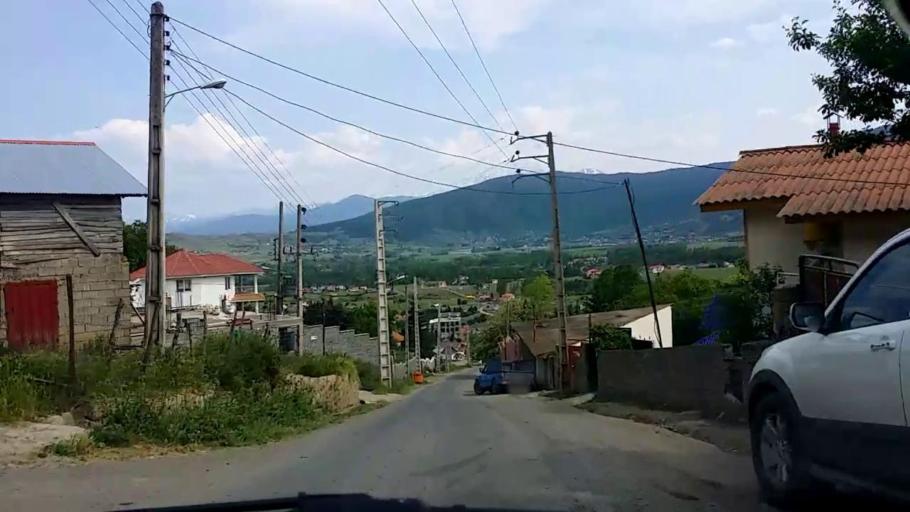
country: IR
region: Mazandaran
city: `Abbasabad
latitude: 36.5507
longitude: 51.1836
